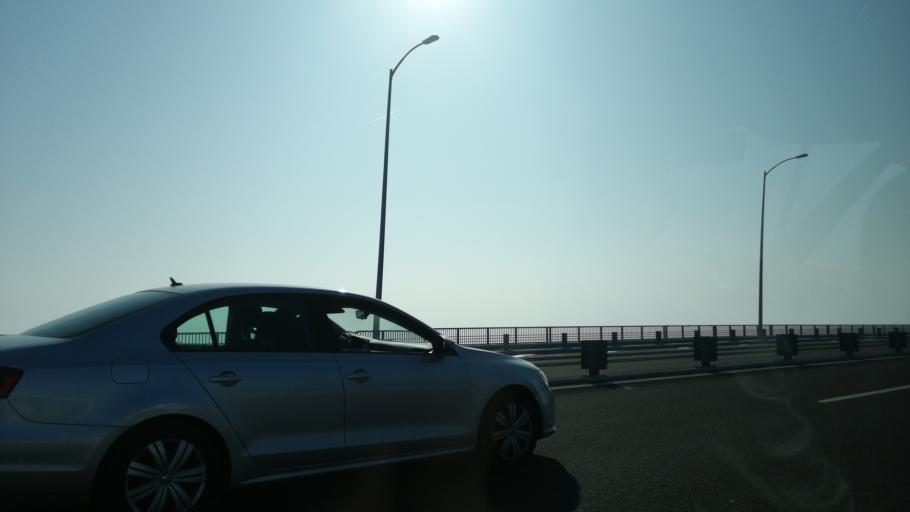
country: TR
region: Yalova
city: Altinova
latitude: 40.7411
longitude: 29.5135
